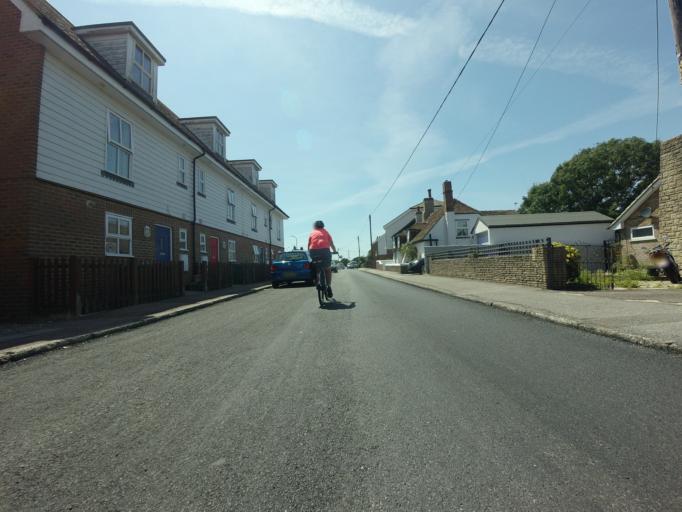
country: GB
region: England
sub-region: Kent
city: Lydd
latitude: 50.9487
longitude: 0.9008
